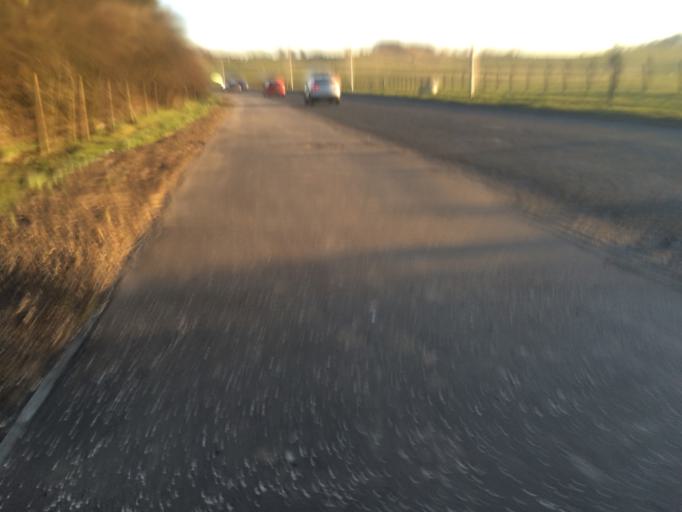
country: GB
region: Scotland
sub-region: Fife
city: Lochgelly
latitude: 56.1423
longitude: -3.3212
